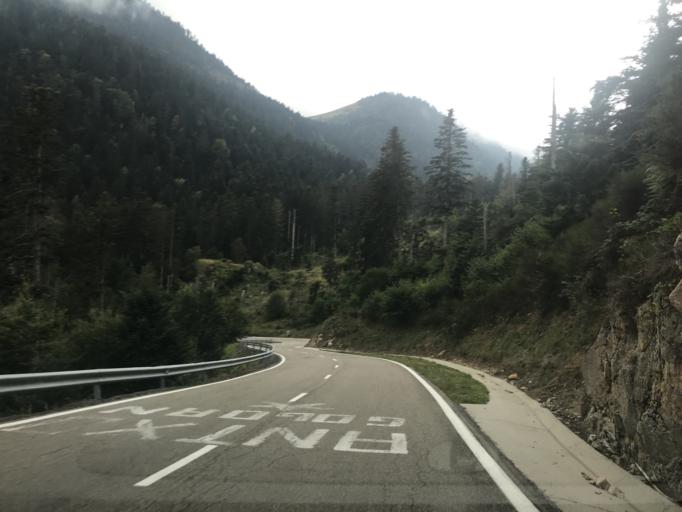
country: ES
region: Catalonia
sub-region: Provincia de Lleida
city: Les
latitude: 42.7665
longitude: 0.6625
